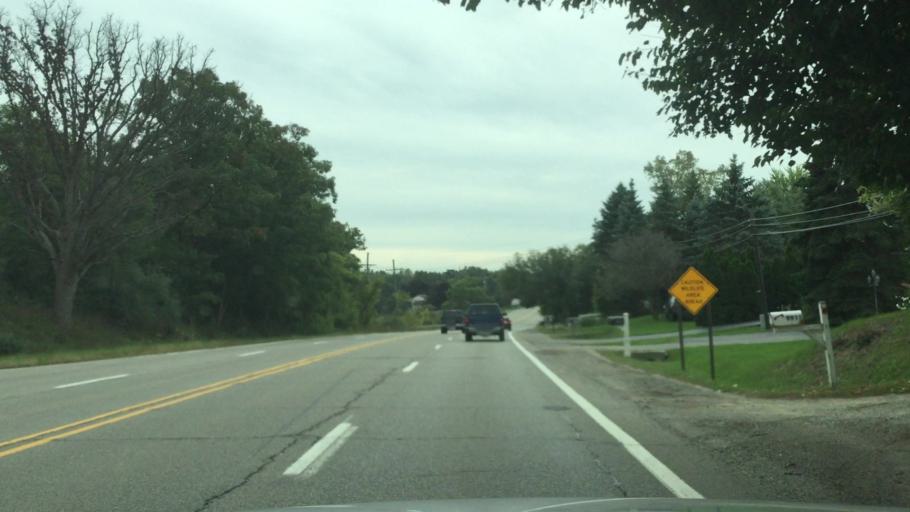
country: US
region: Michigan
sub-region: Oakland County
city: Clarkston
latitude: 42.7650
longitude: -83.4854
